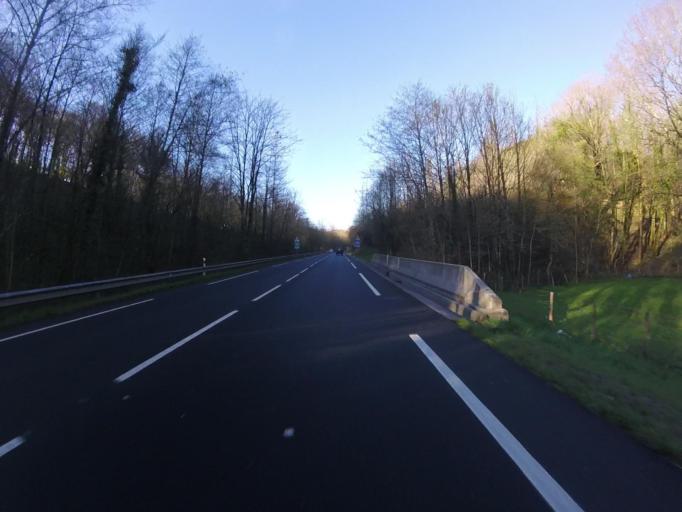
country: ES
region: Basque Country
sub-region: Provincia de Guipuzcoa
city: Errenteria
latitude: 43.2848
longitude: -1.9015
